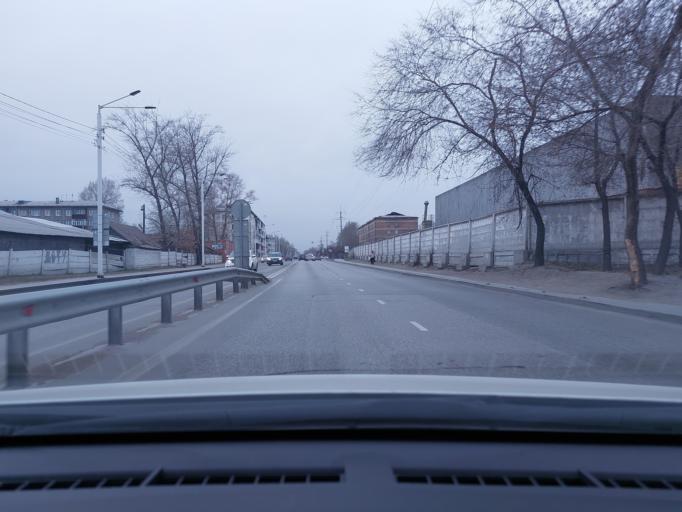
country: RU
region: Irkutsk
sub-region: Irkutskiy Rayon
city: Irkutsk
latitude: 52.3388
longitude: 104.2322
